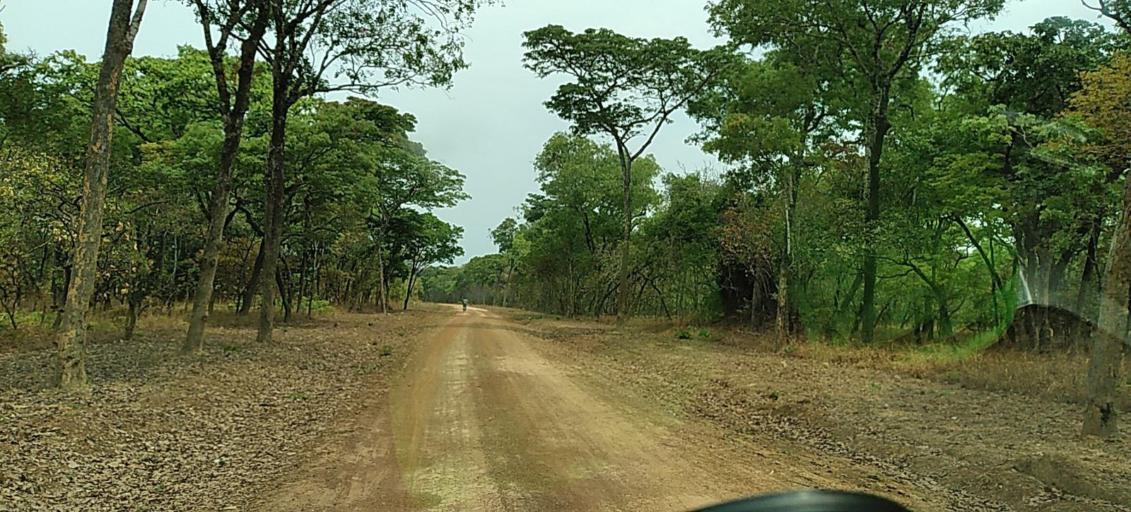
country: ZM
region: North-Western
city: Solwezi
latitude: -12.9484
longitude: 26.5600
